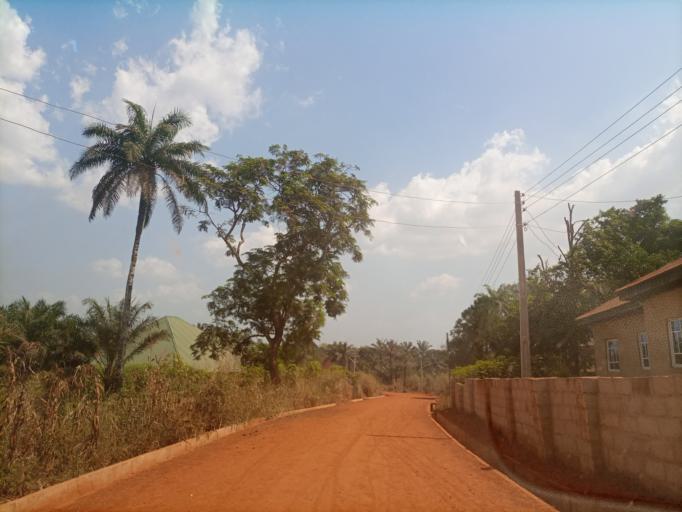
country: NG
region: Enugu
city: Obolo-Eke (1)
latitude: 6.8647
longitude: 7.6592
